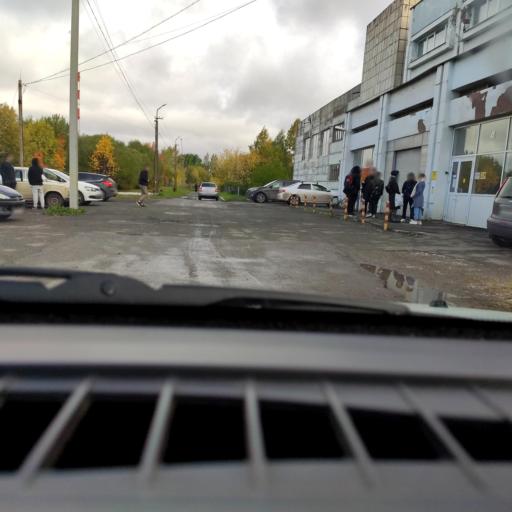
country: RU
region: Perm
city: Froly
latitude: 57.9539
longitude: 56.2704
